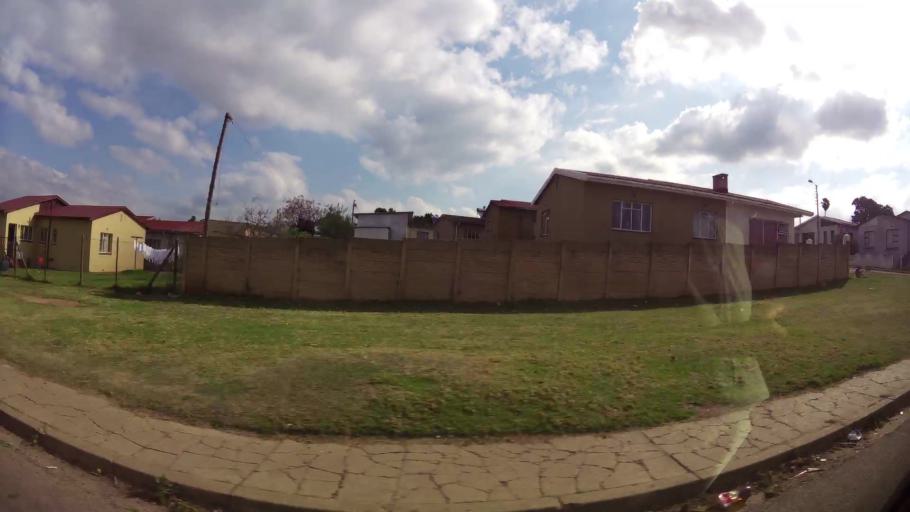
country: ZA
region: Eastern Cape
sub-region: Nelson Mandela Bay Metropolitan Municipality
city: Uitenhage
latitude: -33.7374
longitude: 25.3812
